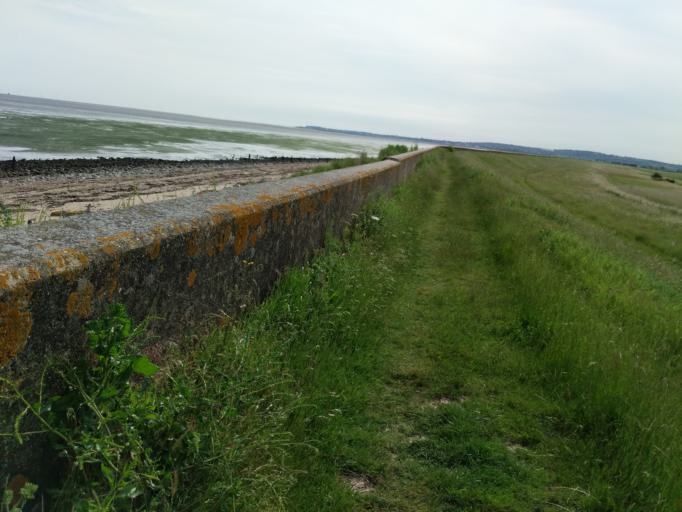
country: GB
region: England
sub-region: Kent
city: Leysdown-on-Sea
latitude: 51.3467
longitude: 0.9376
